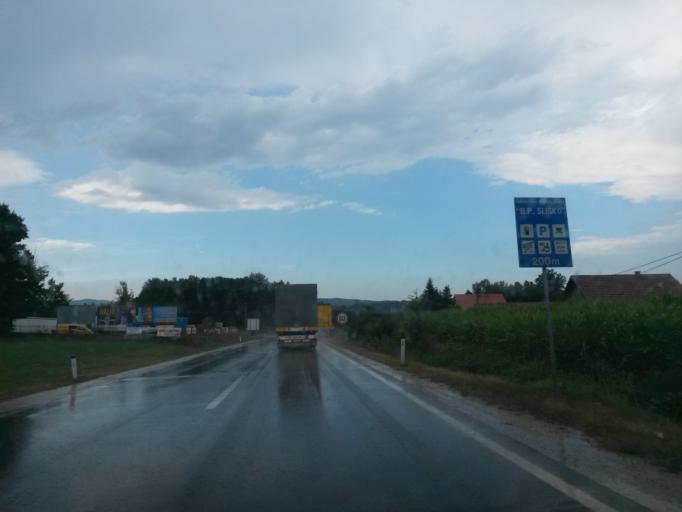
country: BA
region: Federation of Bosnia and Herzegovina
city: Lijesnica
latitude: 44.4758
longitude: 18.0686
